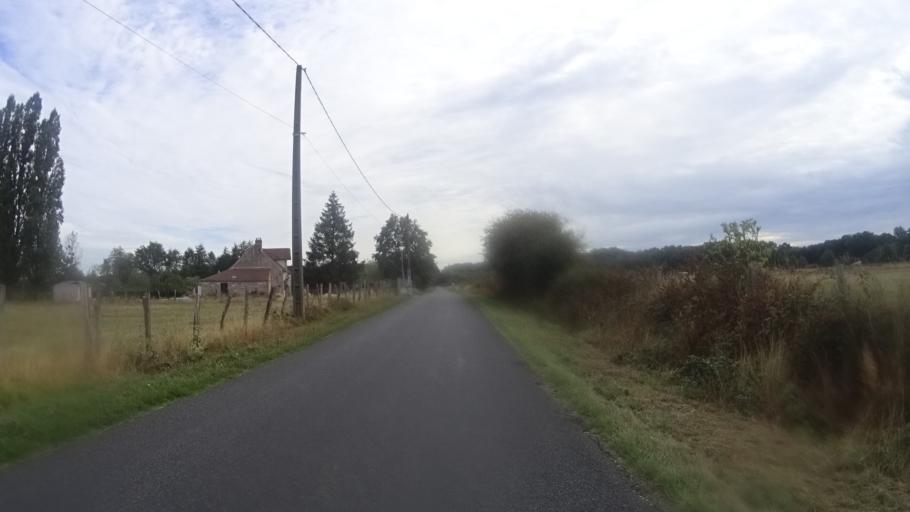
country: FR
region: Centre
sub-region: Departement du Loiret
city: Fay-aux-Loges
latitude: 47.9457
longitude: 2.1665
